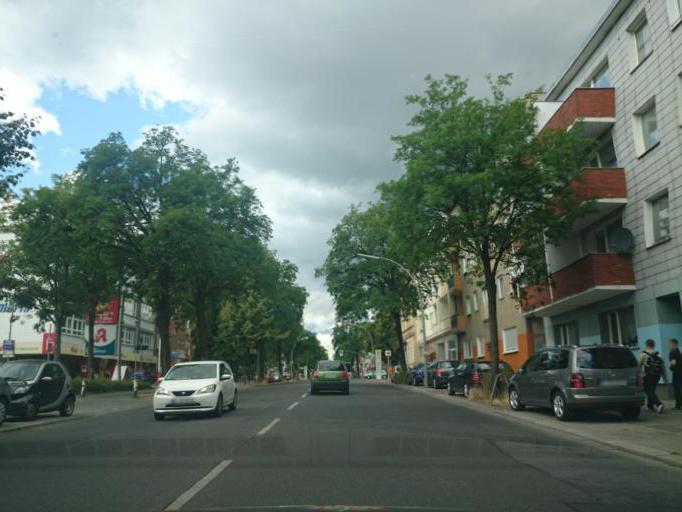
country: DE
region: Berlin
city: Steglitz Bezirk
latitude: 52.4538
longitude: 13.3299
